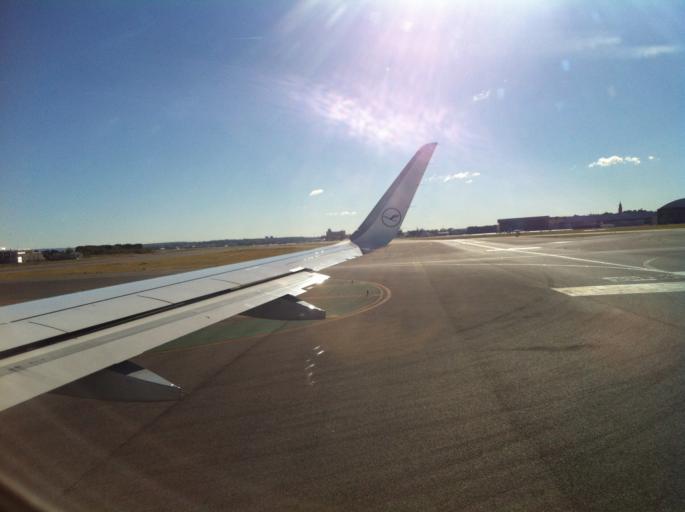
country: ES
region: Madrid
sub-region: Provincia de Madrid
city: Barajas de Madrid
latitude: 40.4886
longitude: -3.5721
